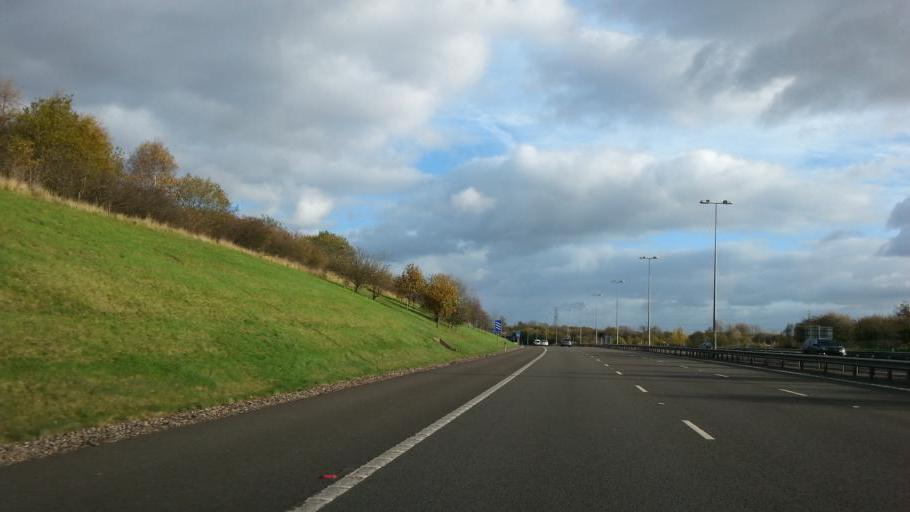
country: GB
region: England
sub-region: Staffordshire
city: Norton Canes
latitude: 52.6633
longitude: -1.9819
